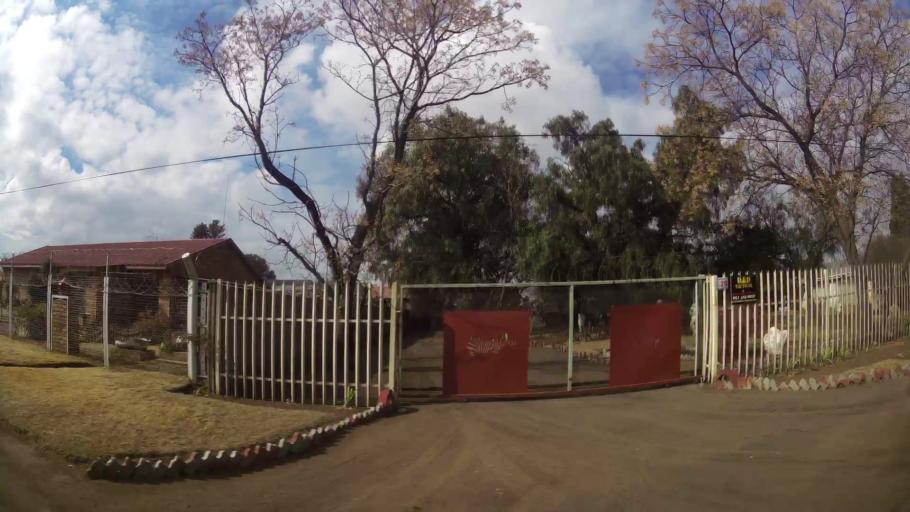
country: ZA
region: Gauteng
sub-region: Sedibeng District Municipality
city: Meyerton
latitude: -26.6054
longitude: 28.0522
